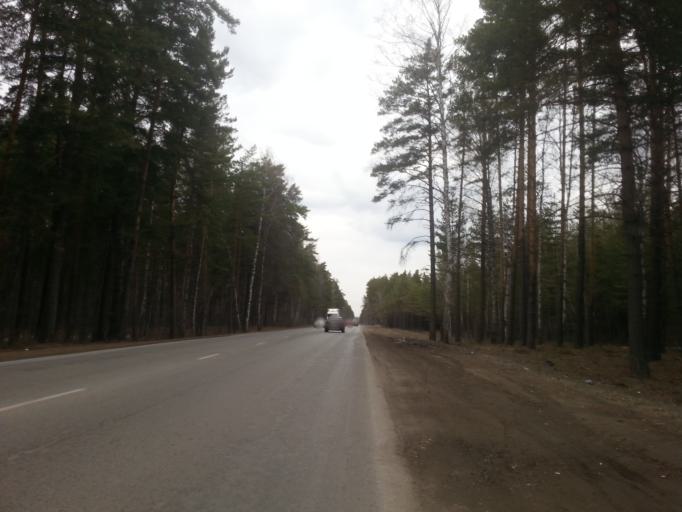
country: RU
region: Altai Krai
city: Yuzhnyy
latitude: 53.2730
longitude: 83.7228
